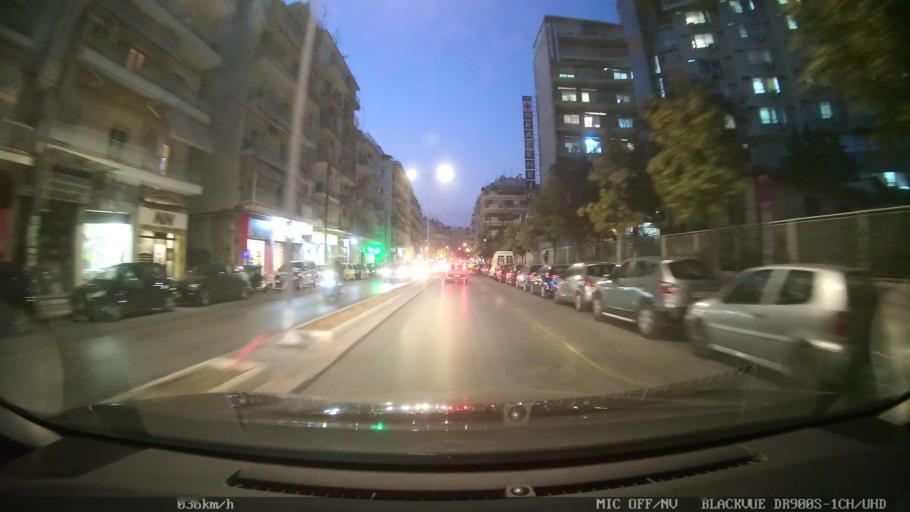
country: GR
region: Central Macedonia
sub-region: Nomos Thessalonikis
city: Triandria
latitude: 40.6173
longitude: 22.9599
